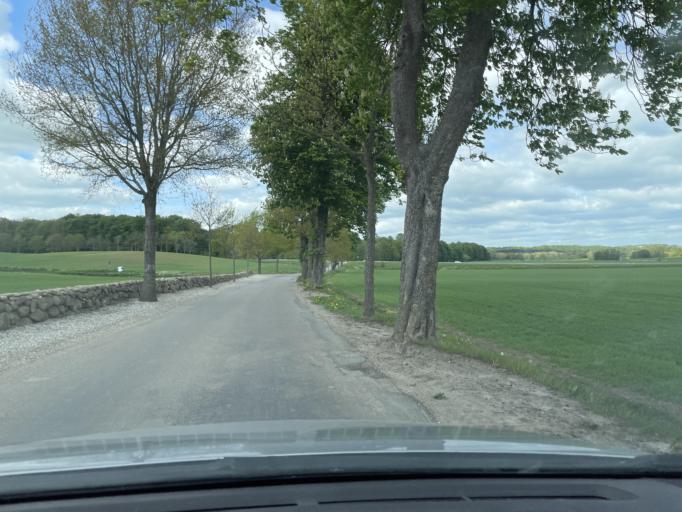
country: DK
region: Central Jutland
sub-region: Odder Kommune
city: Odder
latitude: 55.9132
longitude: 10.1003
